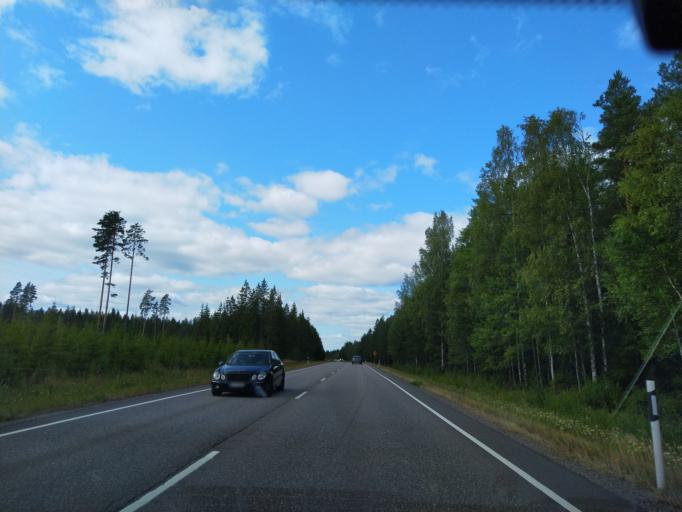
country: FI
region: Haeme
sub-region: Haemeenlinna
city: Renko
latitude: 60.7628
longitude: 24.2749
